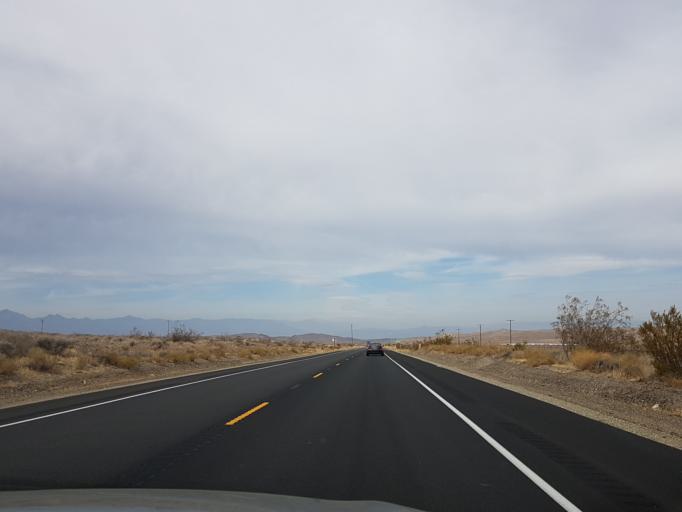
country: US
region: California
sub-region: Kern County
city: Ridgecrest
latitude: 35.4956
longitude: -117.6619
